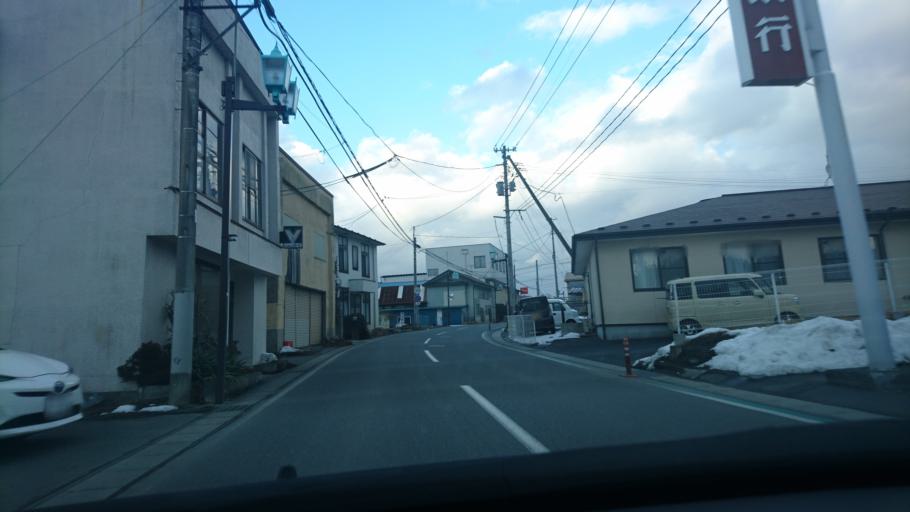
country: JP
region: Iwate
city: Ichinoseki
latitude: 38.9949
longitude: 141.3295
